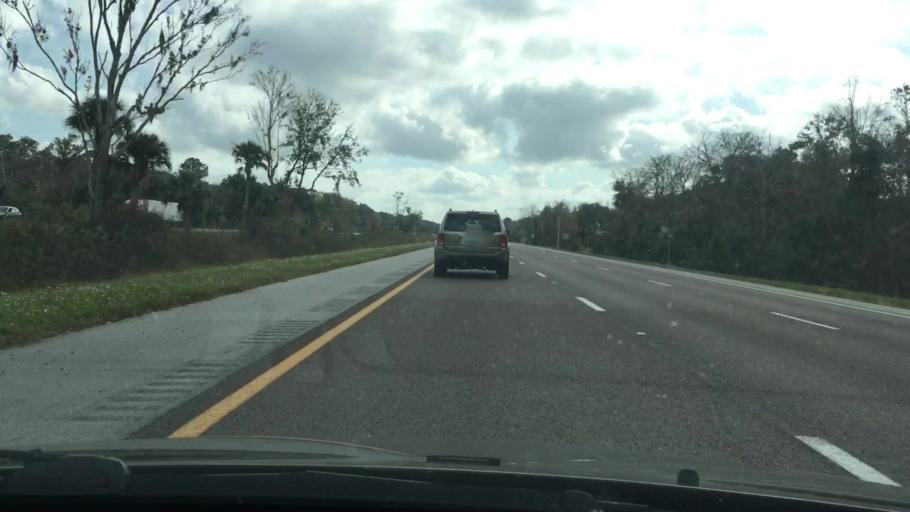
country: US
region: Florida
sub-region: Volusia County
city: Edgewater
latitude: 28.9424
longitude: -80.9471
